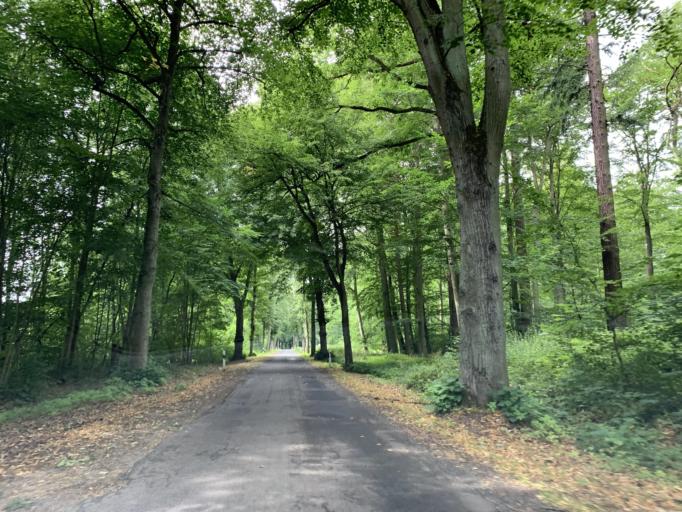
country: DE
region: Mecklenburg-Vorpommern
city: Burg Stargard
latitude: 53.4754
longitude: 13.2819
